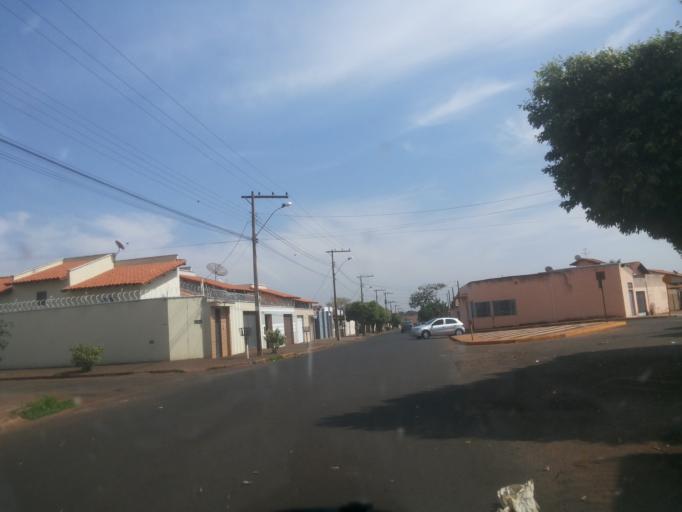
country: BR
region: Minas Gerais
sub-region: Ituiutaba
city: Ituiutaba
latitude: -18.9829
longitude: -49.4838
